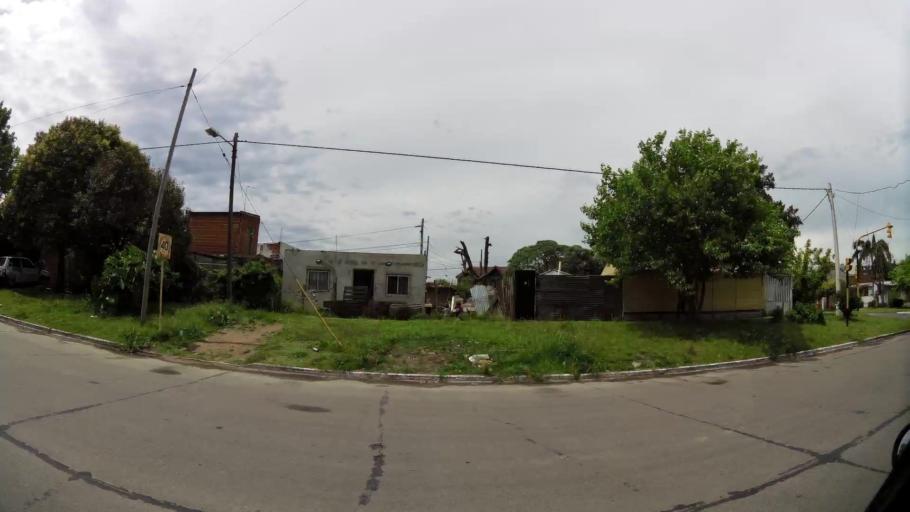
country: AR
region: Buenos Aires
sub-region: Partido de Quilmes
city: Quilmes
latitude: -34.7710
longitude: -58.2356
